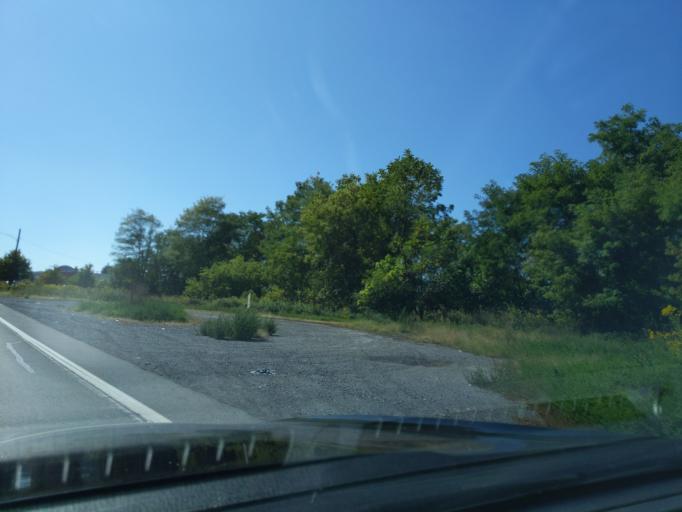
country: US
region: Pennsylvania
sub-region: Blair County
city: Greenwood
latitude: 40.5238
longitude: -78.3668
